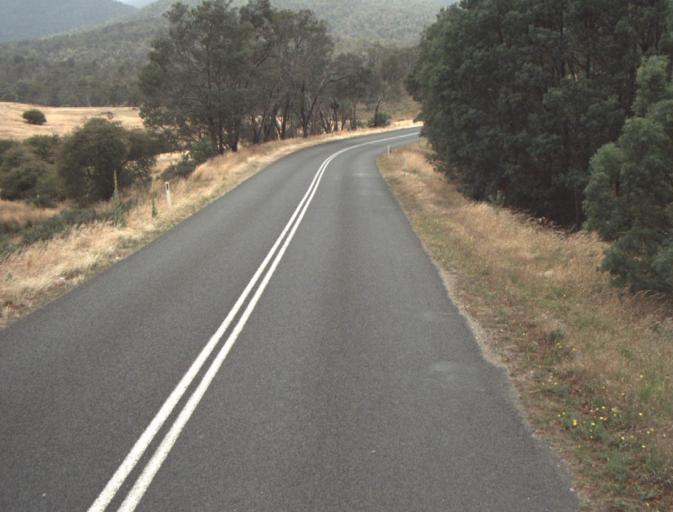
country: AU
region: Tasmania
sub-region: Northern Midlands
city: Evandale
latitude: -41.5076
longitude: 147.3654
